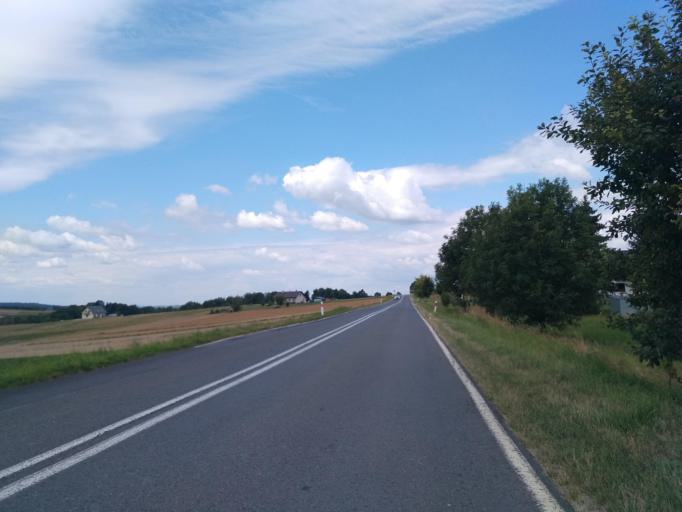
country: PL
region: Subcarpathian Voivodeship
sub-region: Powiat przeworski
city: Jawornik Polski
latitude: 49.8930
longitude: 22.2325
